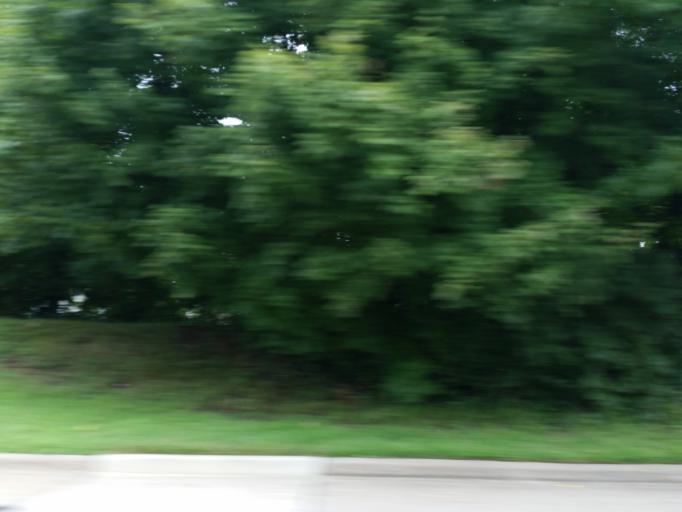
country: US
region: Missouri
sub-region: Cape Girardeau County
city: Cape Girardeau
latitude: 37.3247
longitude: -89.5512
